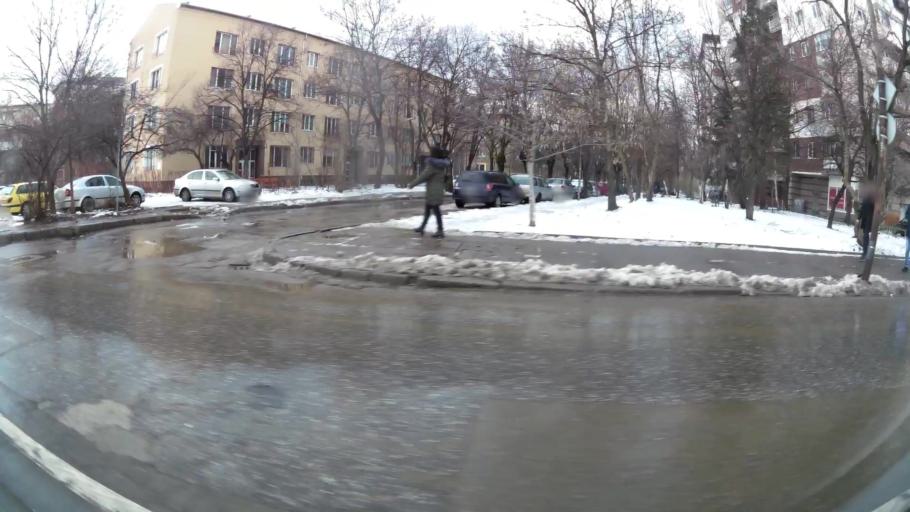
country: BG
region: Sofia-Capital
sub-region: Stolichna Obshtina
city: Sofia
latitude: 42.7041
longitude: 23.2854
